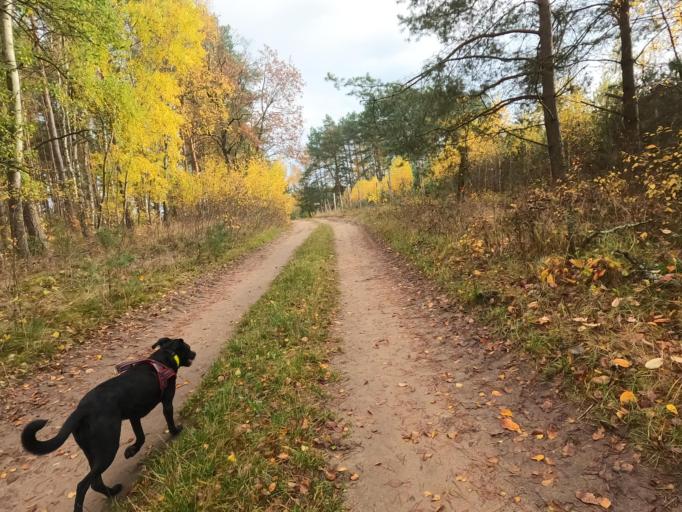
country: PL
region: West Pomeranian Voivodeship
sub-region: Powiat szczecinecki
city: Lubowo
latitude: 53.5414
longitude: 16.4356
